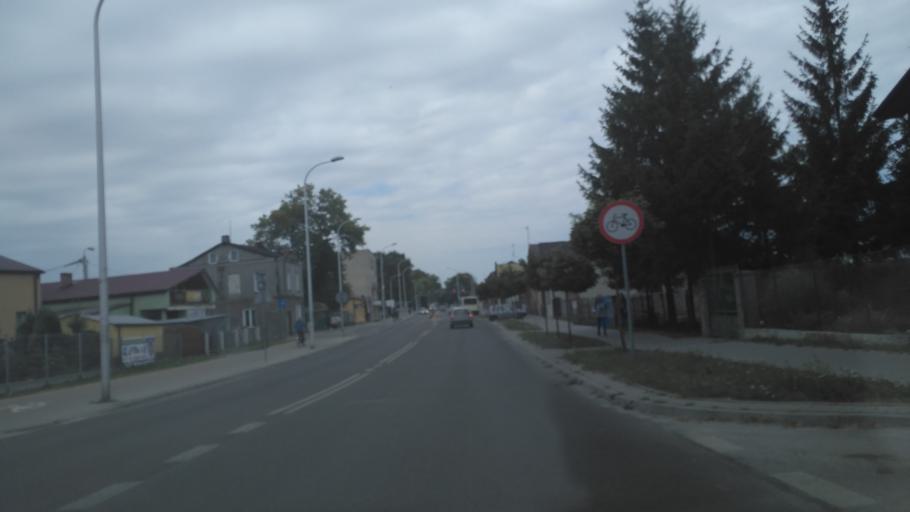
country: PL
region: Lublin Voivodeship
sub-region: Chelm
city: Chelm
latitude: 51.1390
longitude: 23.4583
